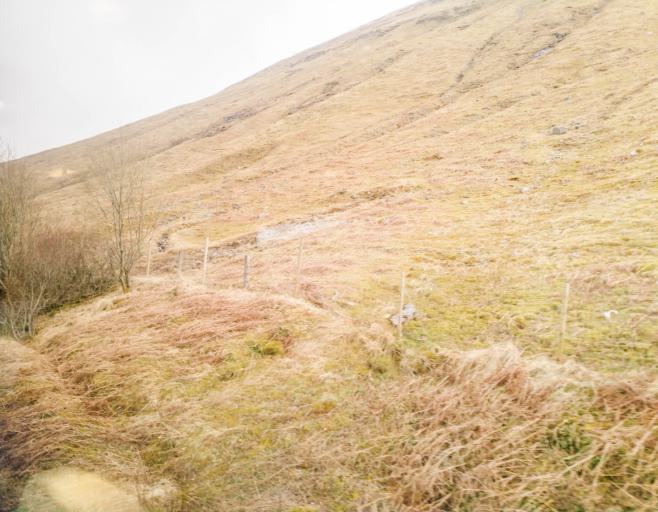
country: GB
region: Scotland
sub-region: Argyll and Bute
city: Garelochhead
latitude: 56.4658
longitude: -4.7155
